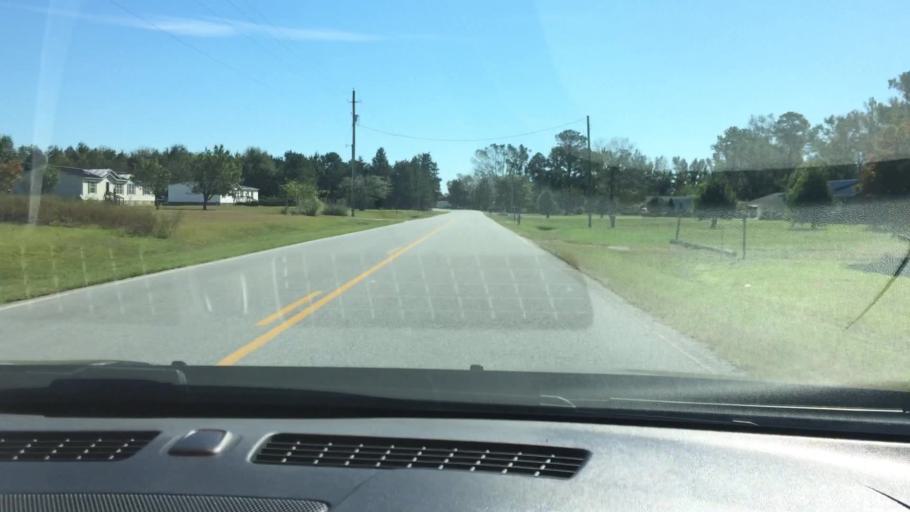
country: US
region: North Carolina
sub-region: Pitt County
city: Grifton
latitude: 35.3793
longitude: -77.3696
